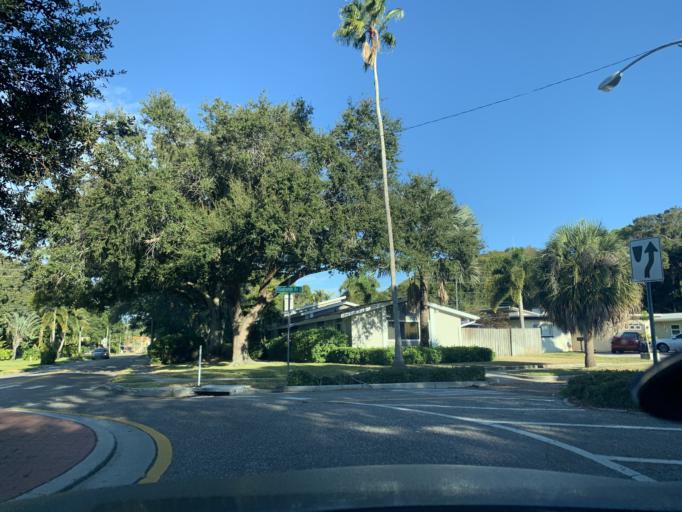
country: US
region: Florida
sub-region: Pinellas County
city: South Pasadena
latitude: 27.7647
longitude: -82.7384
